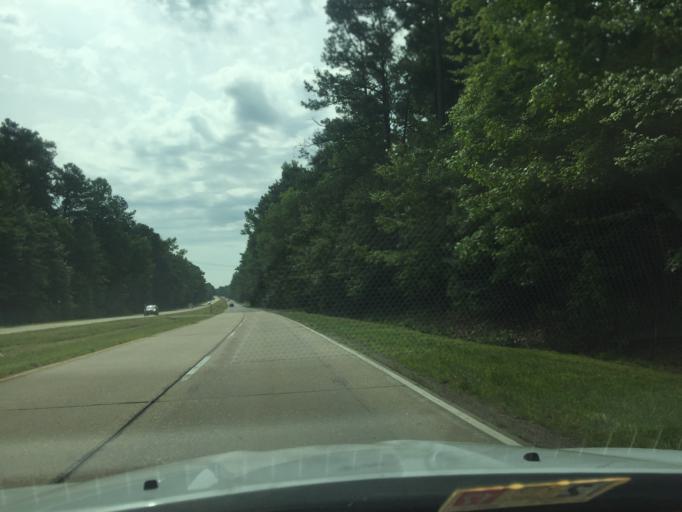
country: US
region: Virginia
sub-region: Charles City County
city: Charles City
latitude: 37.4587
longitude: -77.0964
